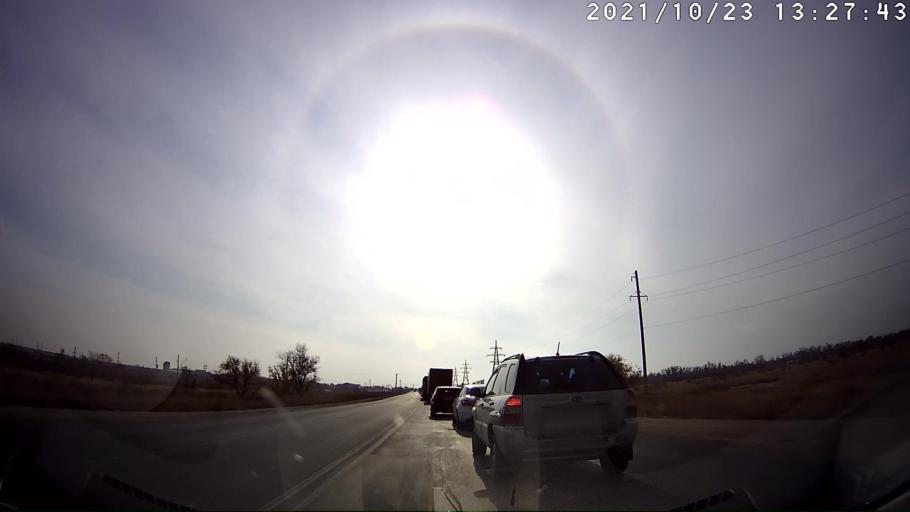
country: RU
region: Volgograd
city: Vodstroy
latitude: 48.8646
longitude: 44.5668
